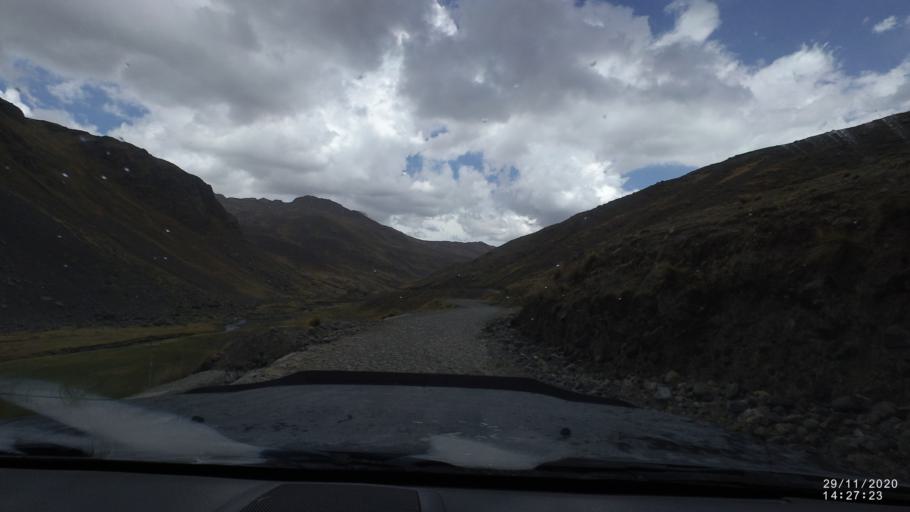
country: BO
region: Cochabamba
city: Sipe Sipe
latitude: -17.2588
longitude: -66.3661
